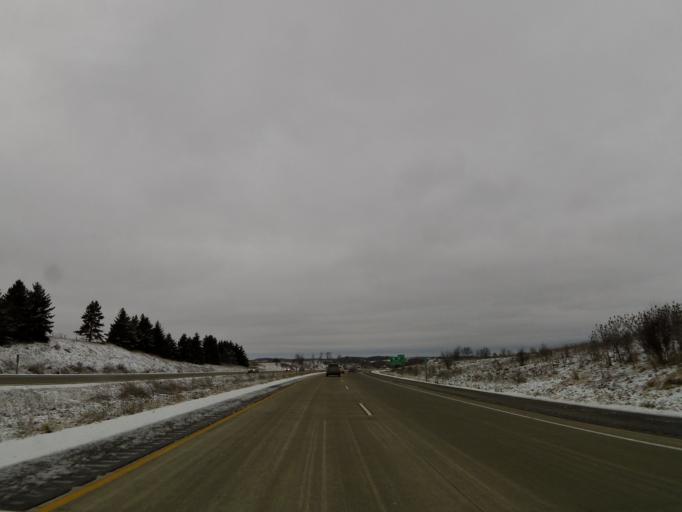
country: US
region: Wisconsin
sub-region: Trempealeau County
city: Osseo
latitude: 44.6365
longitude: -91.2999
